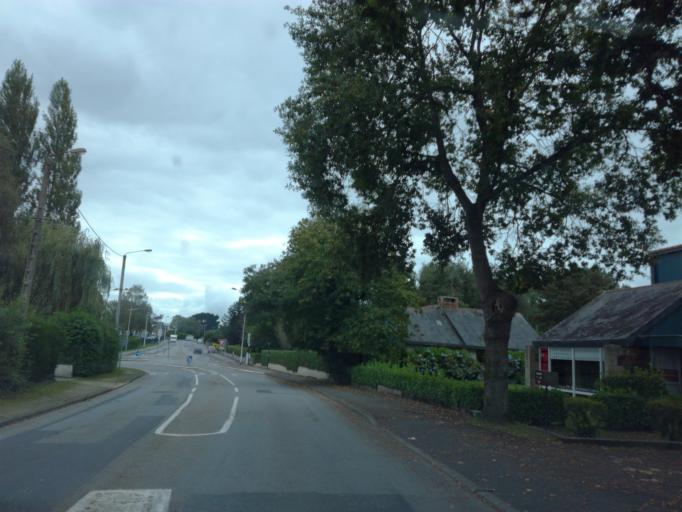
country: FR
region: Brittany
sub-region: Departement des Cotes-d'Armor
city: Loudeac
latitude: 48.1664
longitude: -2.7536
